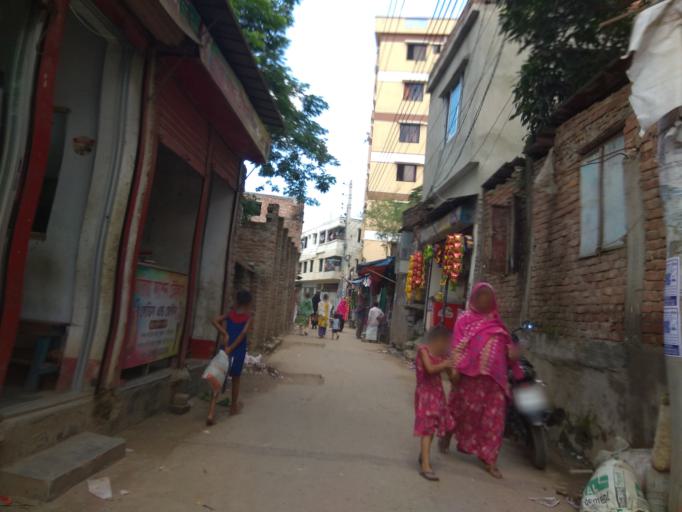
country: BD
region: Dhaka
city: Tungi
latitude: 23.8274
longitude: 90.3907
